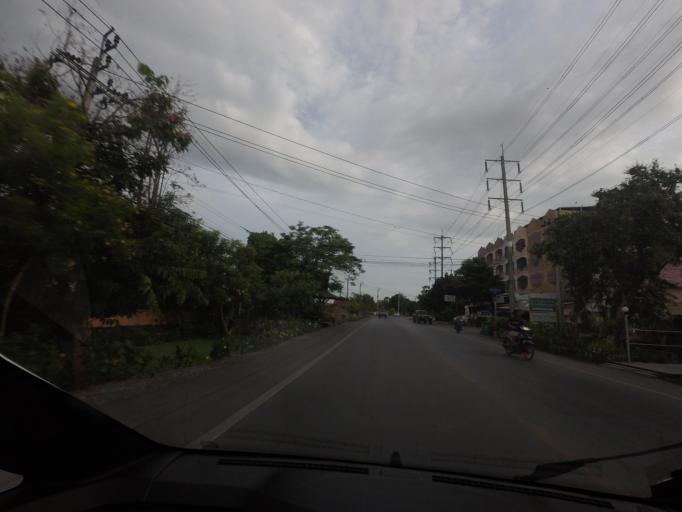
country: TH
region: Bangkok
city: Nong Chok
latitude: 13.8701
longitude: 100.8628
